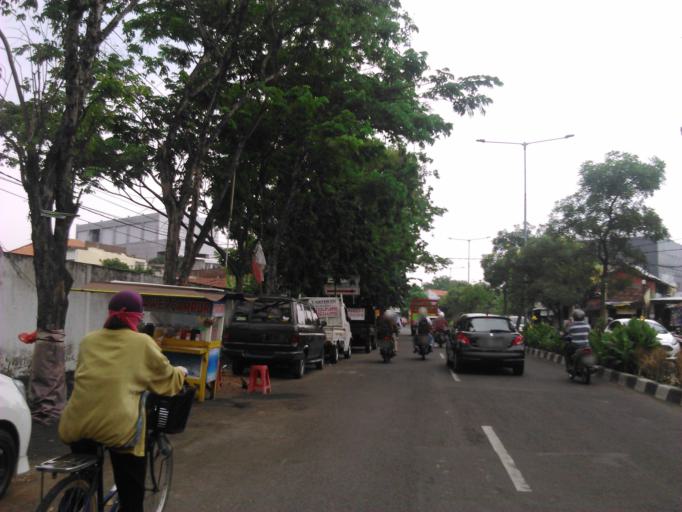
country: ID
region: East Java
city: Gubengairlangga
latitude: -7.2727
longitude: 112.7614
